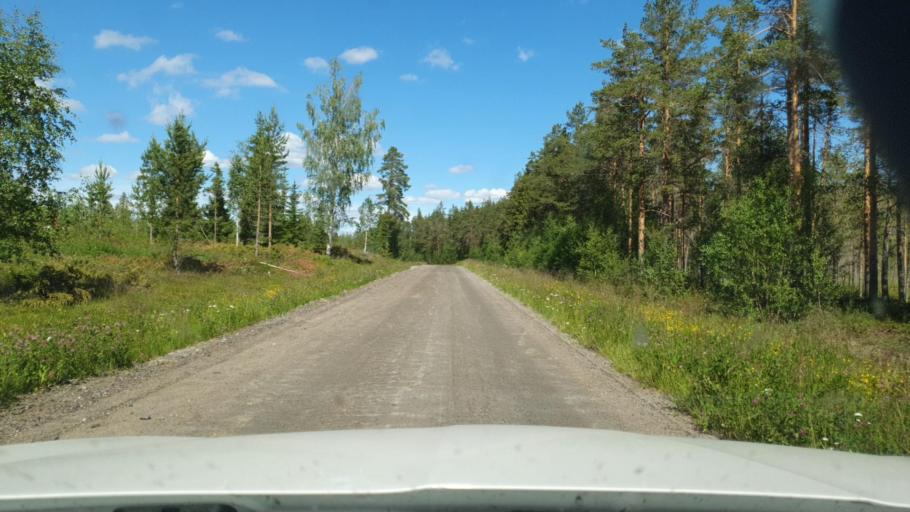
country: SE
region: Vaesterbotten
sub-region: Skelleftea Kommun
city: Byske
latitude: 65.1261
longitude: 21.2037
